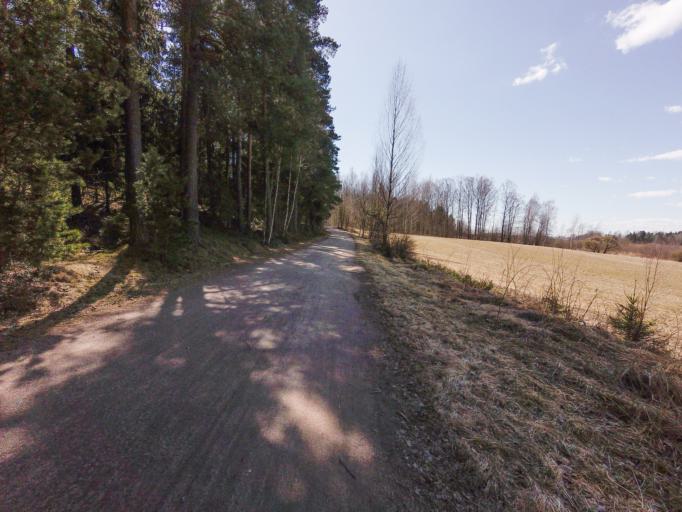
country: FI
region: Uusimaa
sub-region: Helsinki
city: Vantaa
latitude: 60.2168
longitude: 25.0265
